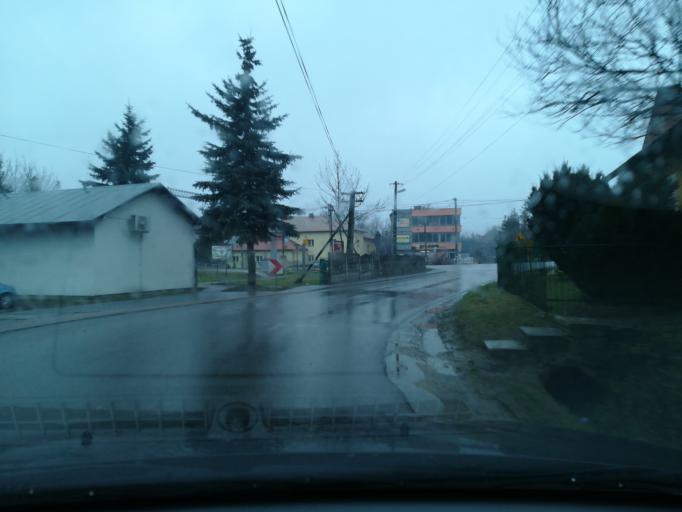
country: PL
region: Subcarpathian Voivodeship
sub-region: Powiat lancucki
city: Kosina
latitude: 50.0709
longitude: 22.3297
